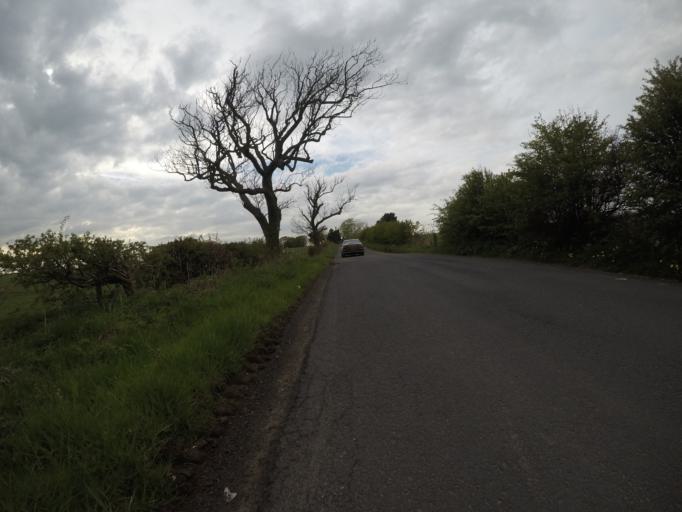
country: GB
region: Scotland
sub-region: East Ayrshire
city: Kilmarnock
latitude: 55.6447
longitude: -4.4829
